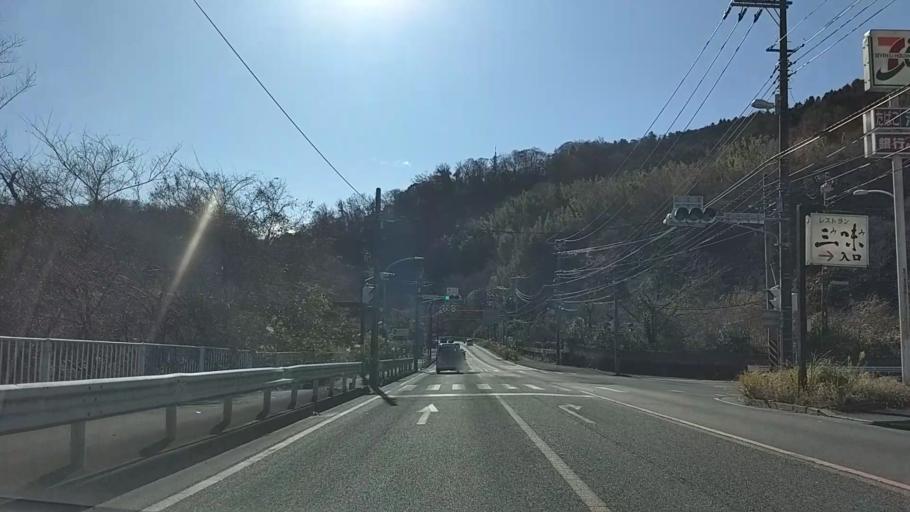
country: JP
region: Kanagawa
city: Hadano
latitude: 35.3632
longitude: 139.1587
